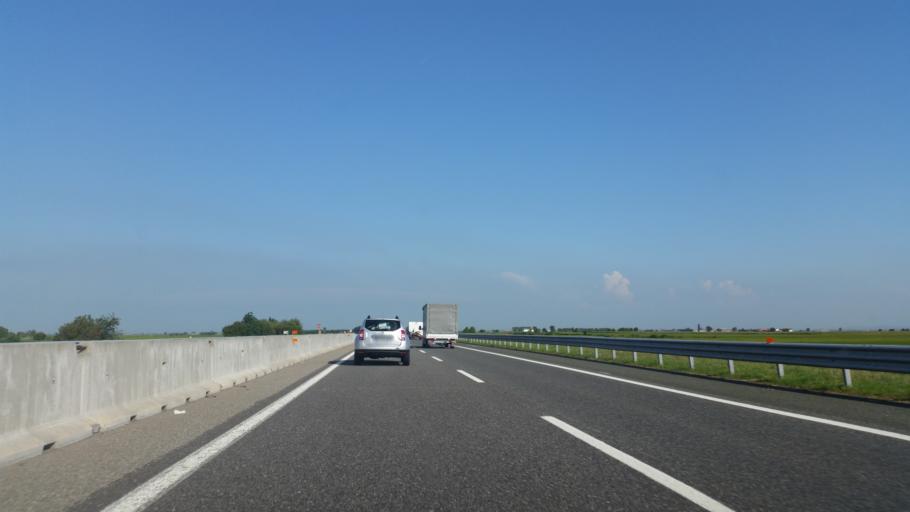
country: IT
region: Piedmont
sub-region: Provincia di Vercelli
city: Salasco
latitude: 45.3215
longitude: 8.2529
